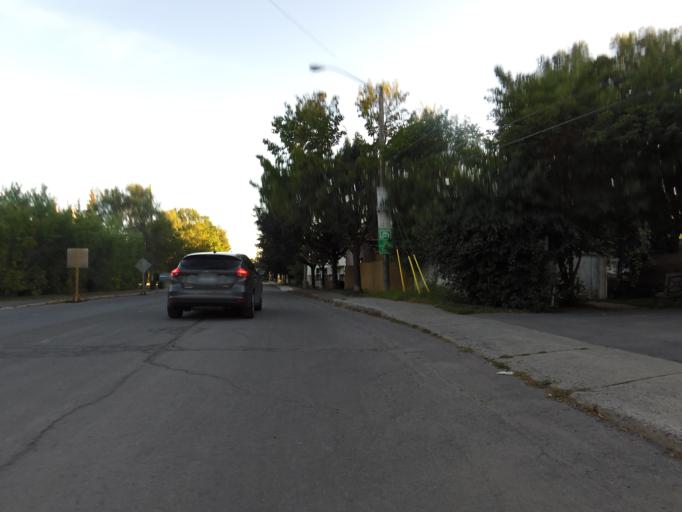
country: CA
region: Ontario
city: Ottawa
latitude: 45.4332
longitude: -75.6609
